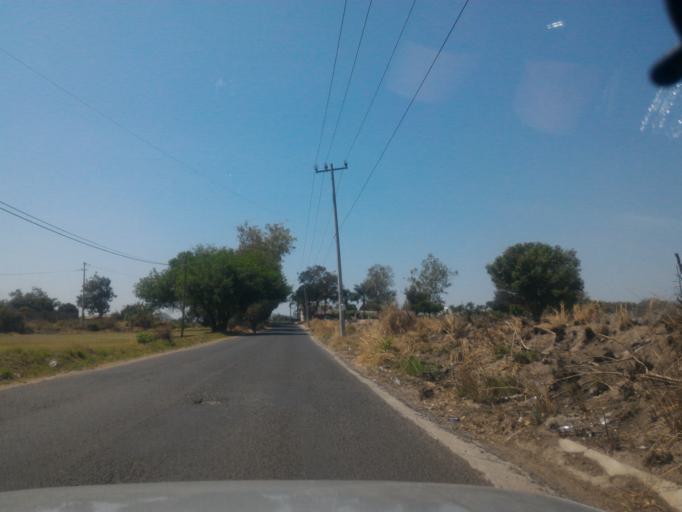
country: MX
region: Jalisco
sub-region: San Pedro Tlaquepaque
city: Santa Anita
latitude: 20.5571
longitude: -103.4252
